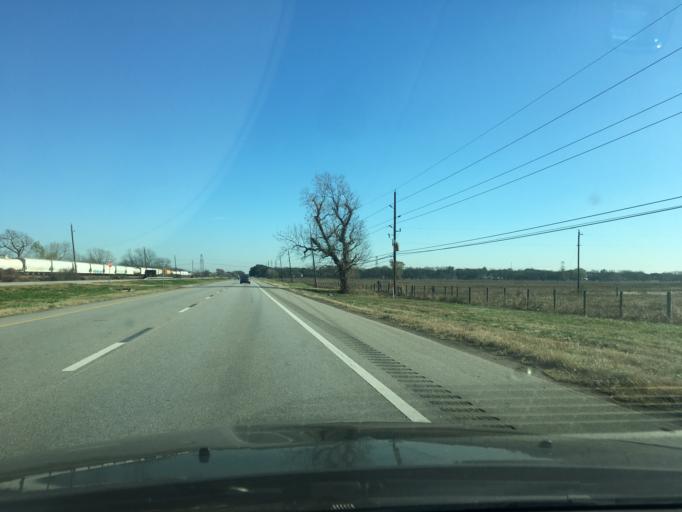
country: US
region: Texas
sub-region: Fort Bend County
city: New Territory
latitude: 29.5995
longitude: -95.7046
